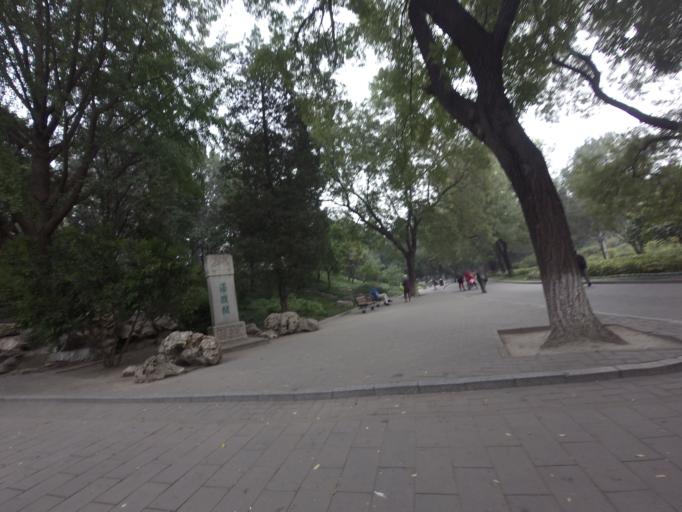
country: CN
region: Beijing
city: Jingshan
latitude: 39.9281
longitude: 116.3859
